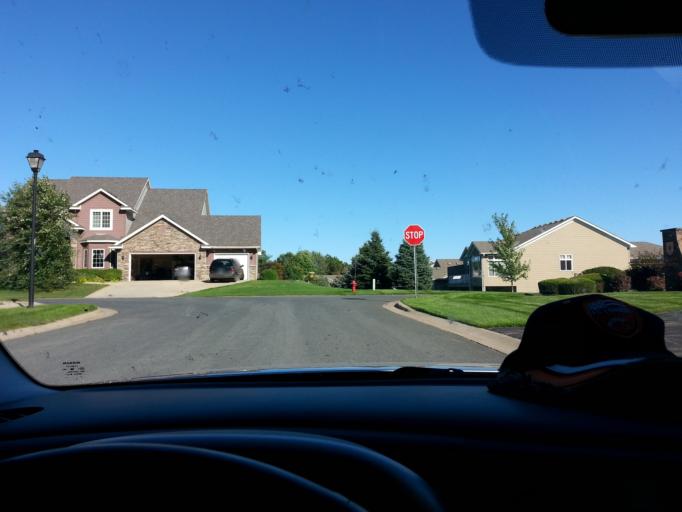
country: US
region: Minnesota
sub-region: Scott County
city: Prior Lake
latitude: 44.7283
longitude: -93.4443
